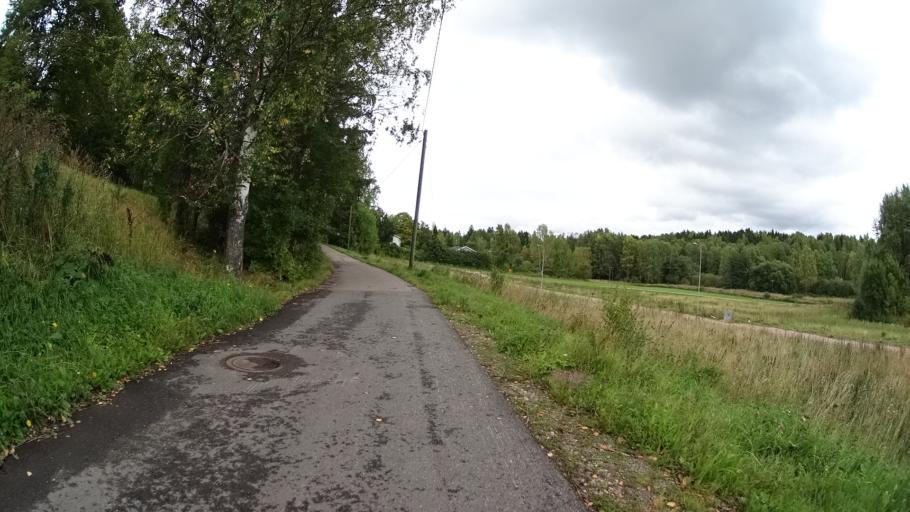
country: FI
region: Uusimaa
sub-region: Helsinki
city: Kauniainen
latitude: 60.2316
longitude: 24.6982
